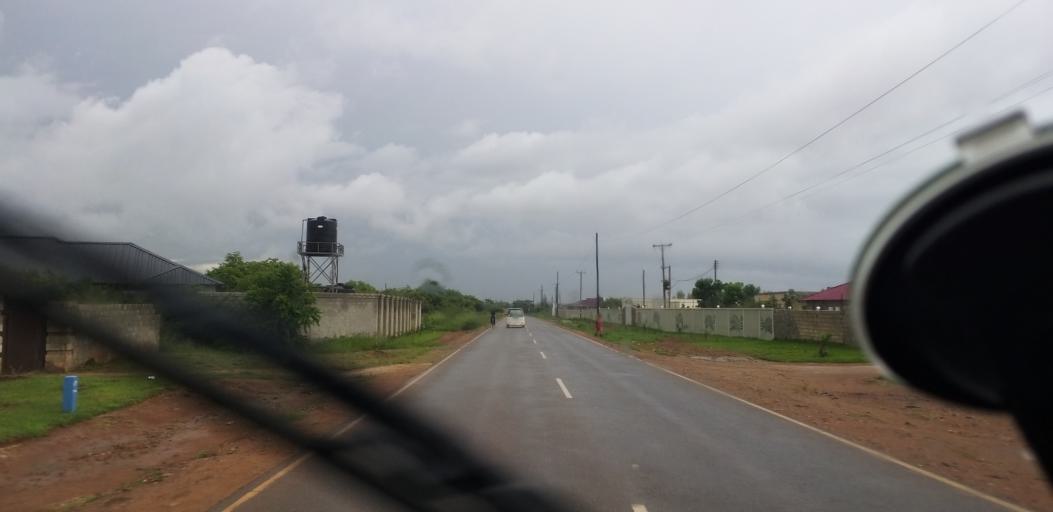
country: ZM
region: Lusaka
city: Lusaka
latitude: -15.4945
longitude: 28.3131
